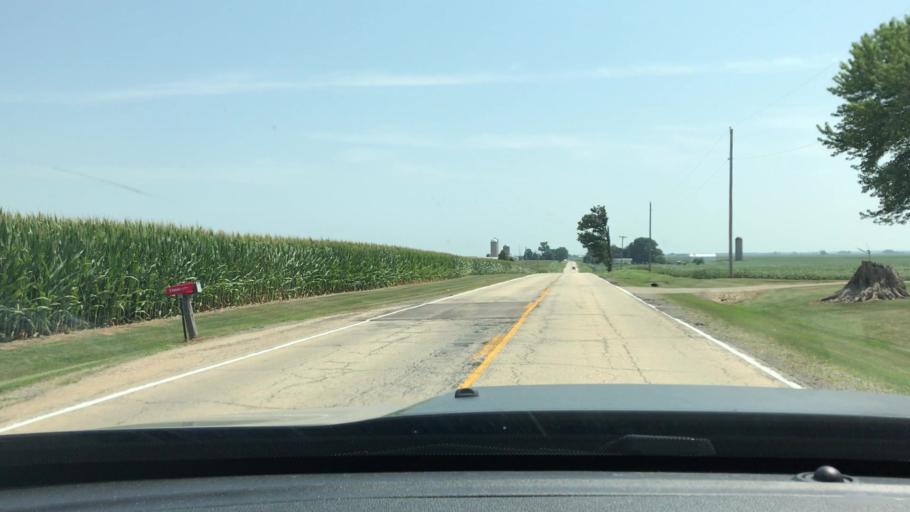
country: US
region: Illinois
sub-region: LaSalle County
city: Earlville
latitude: 41.4690
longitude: -88.9263
